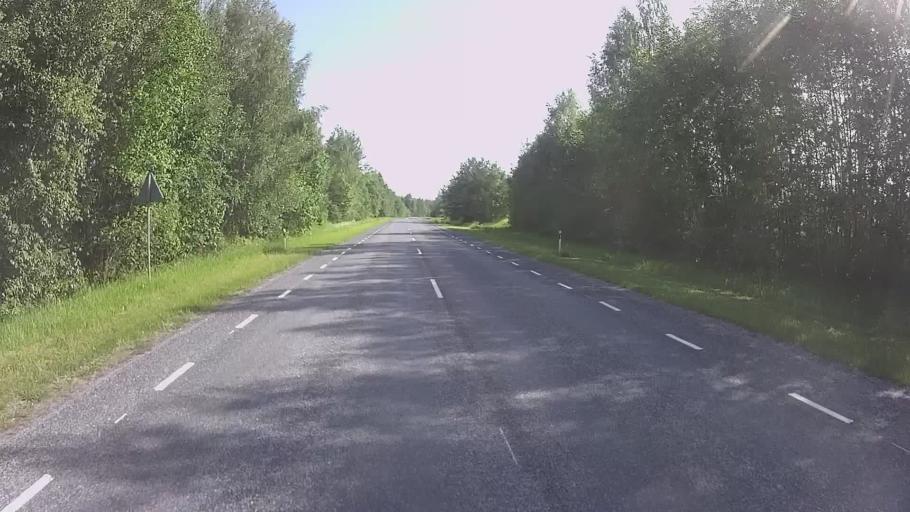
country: EE
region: Valgamaa
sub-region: Torva linn
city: Torva
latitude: 58.0417
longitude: 25.9735
